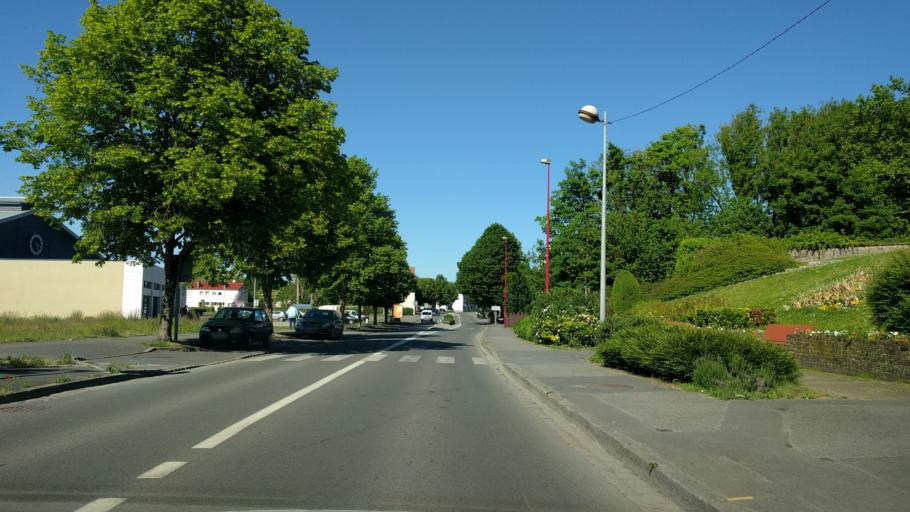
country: FR
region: Picardie
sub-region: Departement de la Somme
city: Peronne
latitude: 49.9315
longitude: 2.9383
